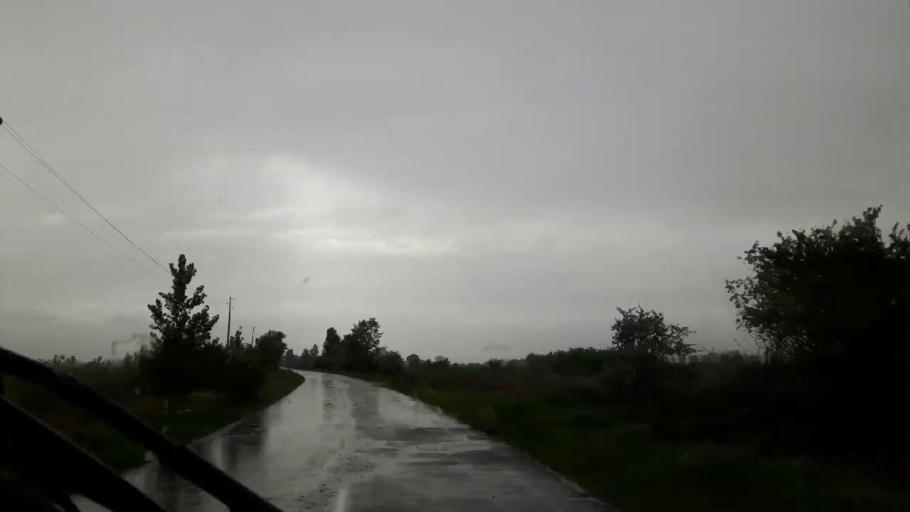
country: GE
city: Agara
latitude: 42.0144
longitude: 43.8065
